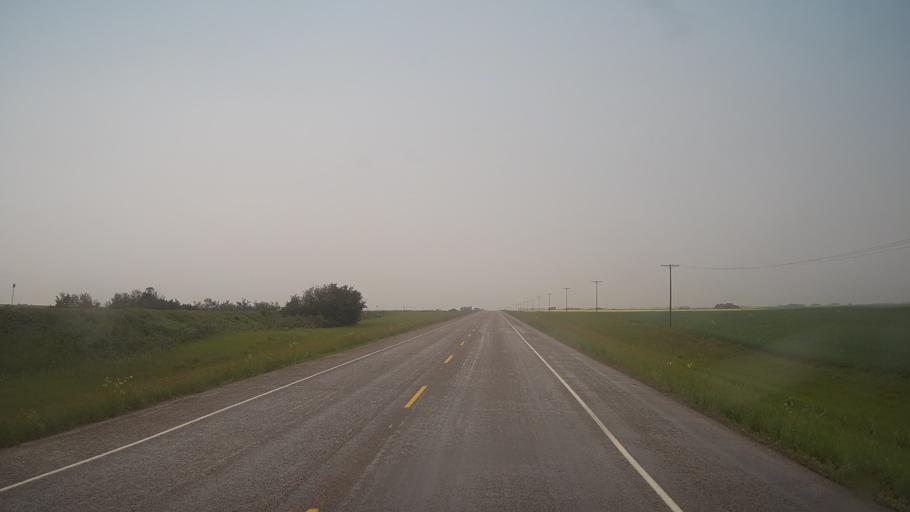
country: CA
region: Saskatchewan
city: Biggar
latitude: 52.1459
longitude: -108.2105
